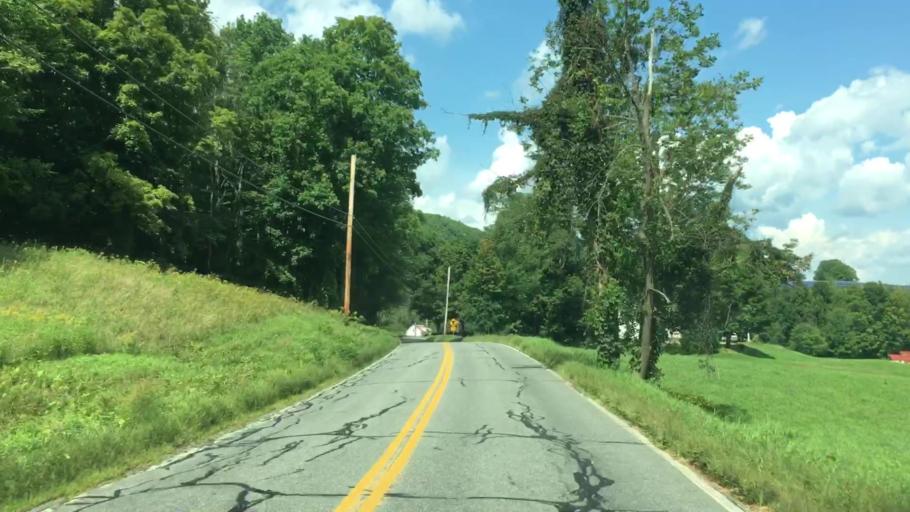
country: US
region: Vermont
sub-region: Windham County
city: West Brattleboro
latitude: 42.7981
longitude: -72.5986
